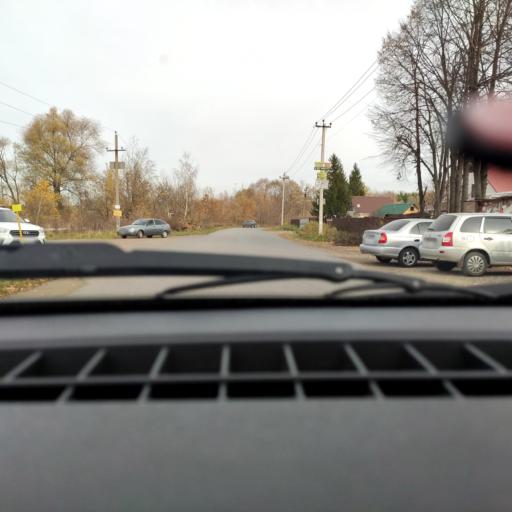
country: RU
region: Bashkortostan
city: Iglino
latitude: 54.8115
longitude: 56.1897
